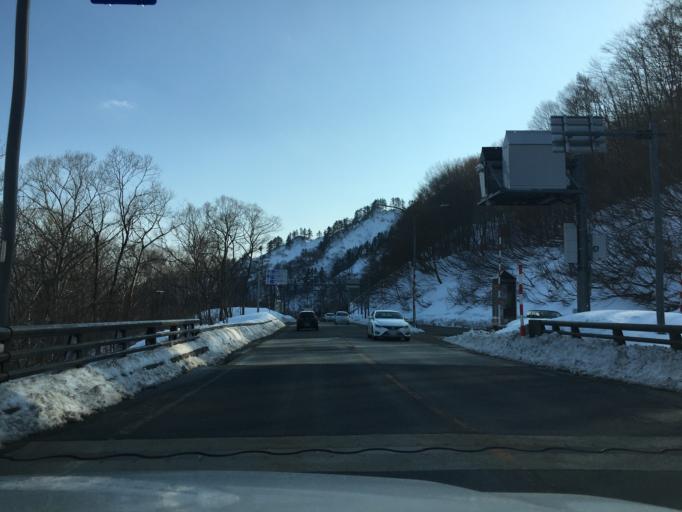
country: JP
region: Yamagata
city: Sagae
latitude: 38.4624
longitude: 139.9914
